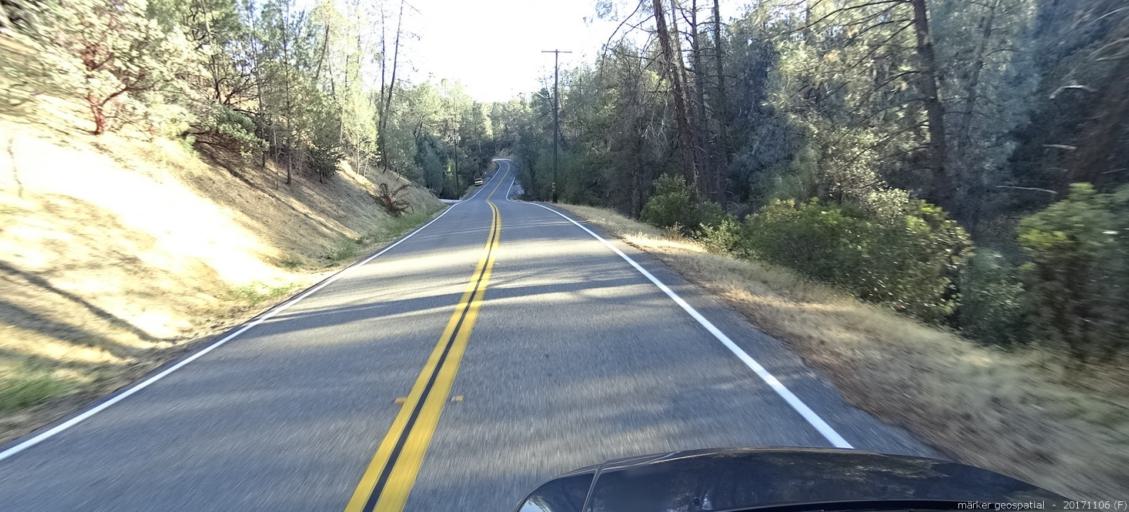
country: US
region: California
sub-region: Shasta County
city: Shasta
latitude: 40.5715
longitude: -122.4746
